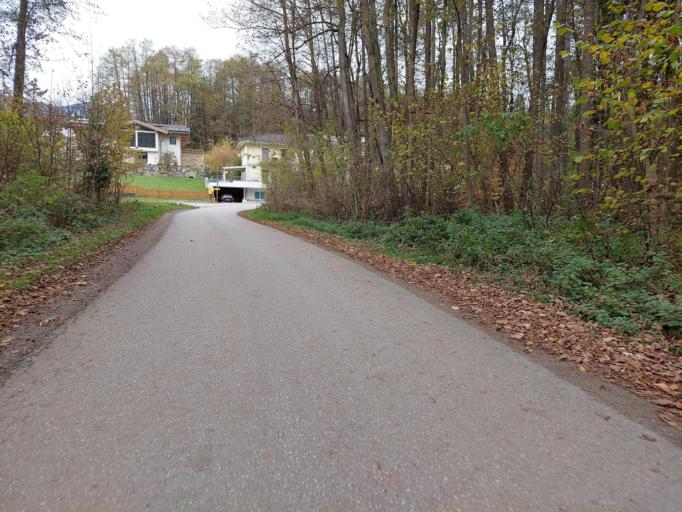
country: AT
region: Tyrol
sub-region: Politischer Bezirk Kufstein
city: Angath
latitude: 47.4964
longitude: 12.0504
